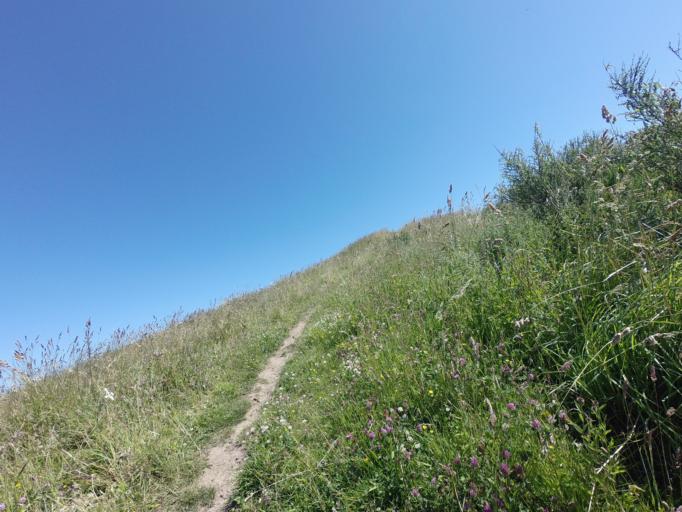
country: GB
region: Scotland
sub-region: West Lothian
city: West Calder
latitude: 55.8836
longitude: -3.5939
